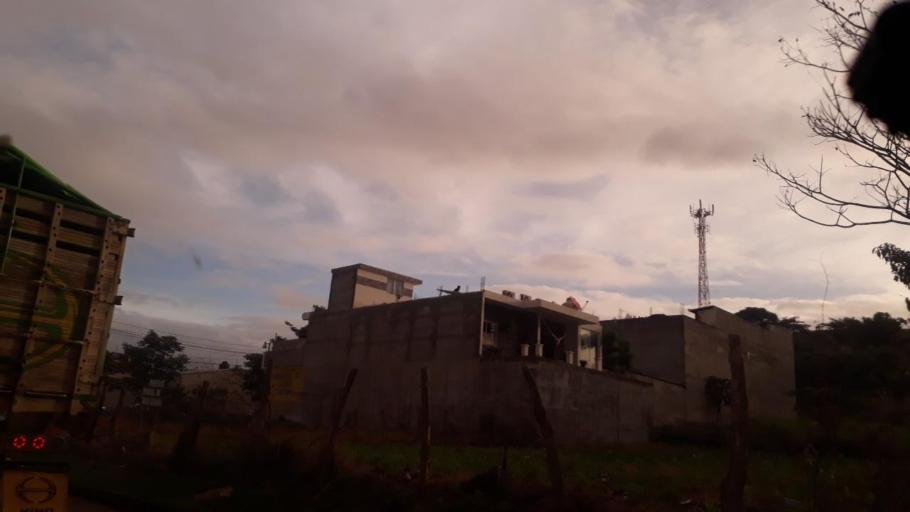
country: GT
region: Jutiapa
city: El Progreso
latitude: 14.3549
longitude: -89.8448
